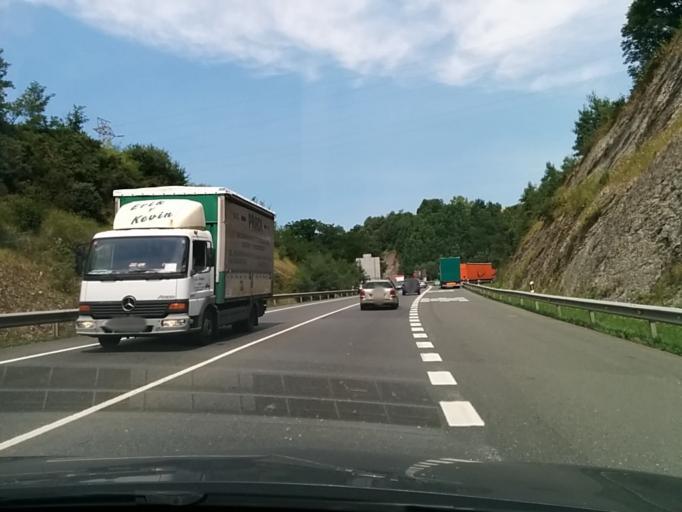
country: ES
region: Basque Country
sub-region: Provincia de Guipuzcoa
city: Errenteria
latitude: 43.3122
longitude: -1.8915
